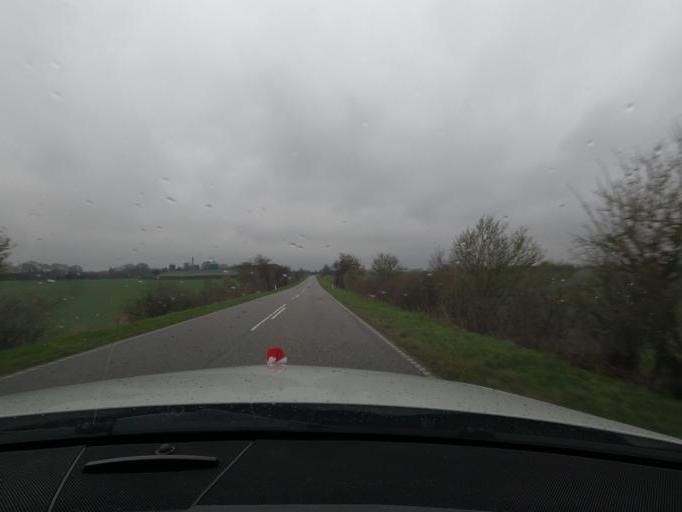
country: DK
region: South Denmark
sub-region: Haderslev Kommune
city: Starup
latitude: 55.2456
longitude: 9.6725
